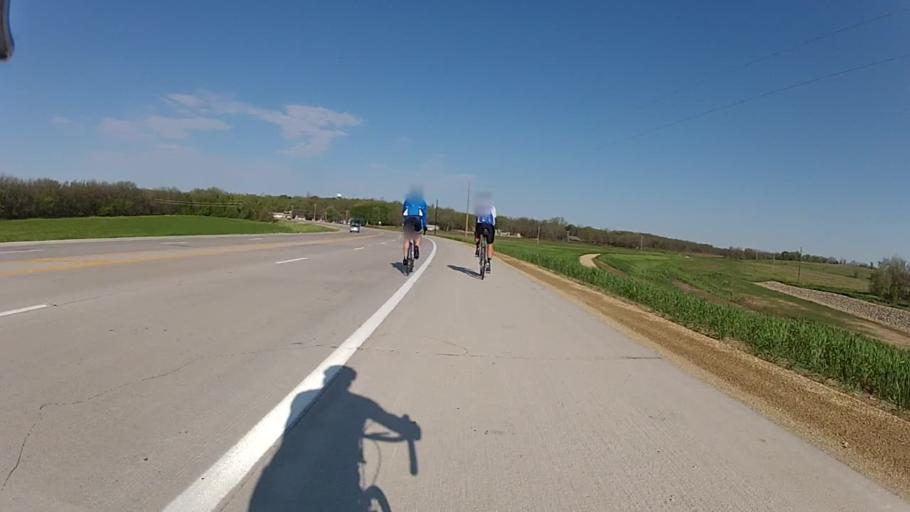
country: US
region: Kansas
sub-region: Riley County
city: Ogden
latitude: 39.1185
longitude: -96.7023
